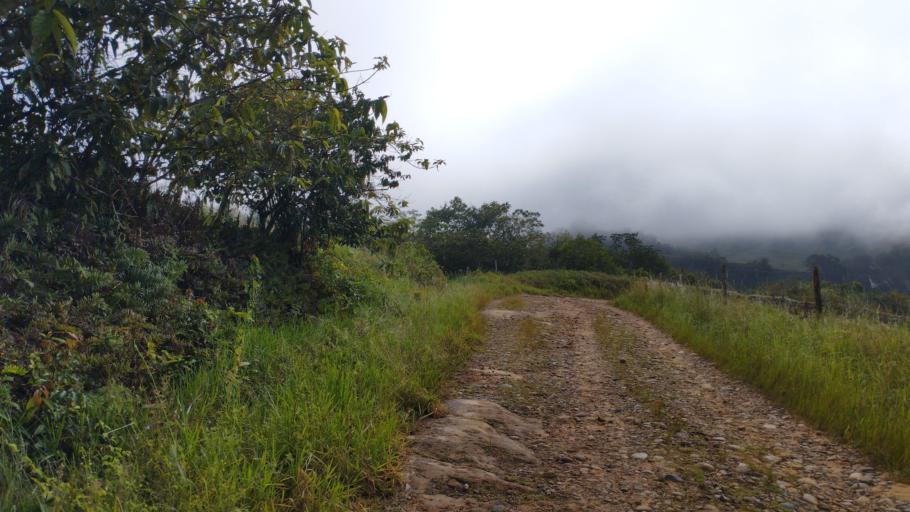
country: CO
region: Casanare
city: Sabanalarga
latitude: 4.7657
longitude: -73.0784
